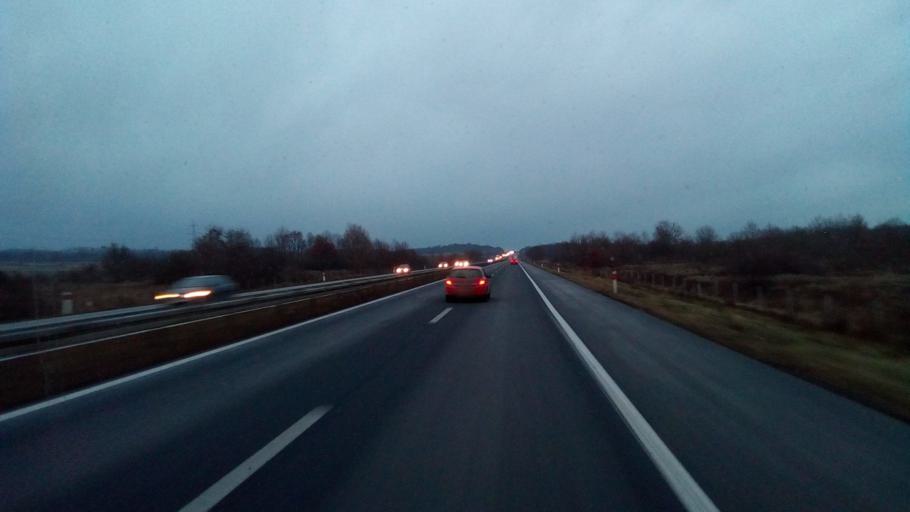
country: HR
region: Zagrebacka
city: Brckovljani
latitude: 45.8824
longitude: 16.2247
